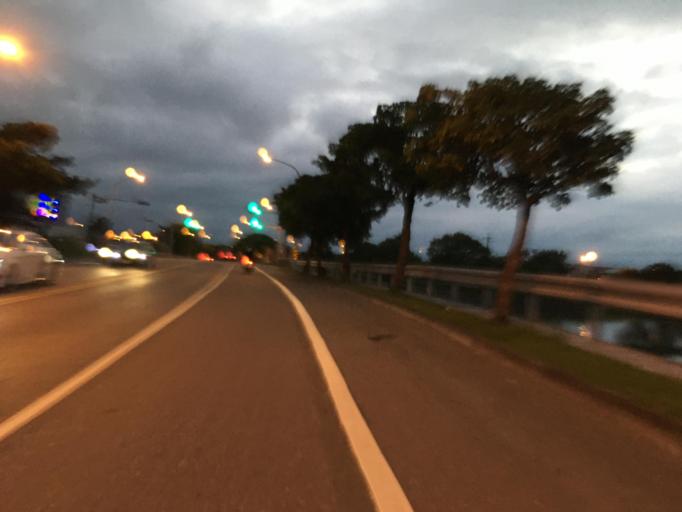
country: TW
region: Taiwan
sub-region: Yilan
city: Yilan
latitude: 24.6735
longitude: 121.8008
